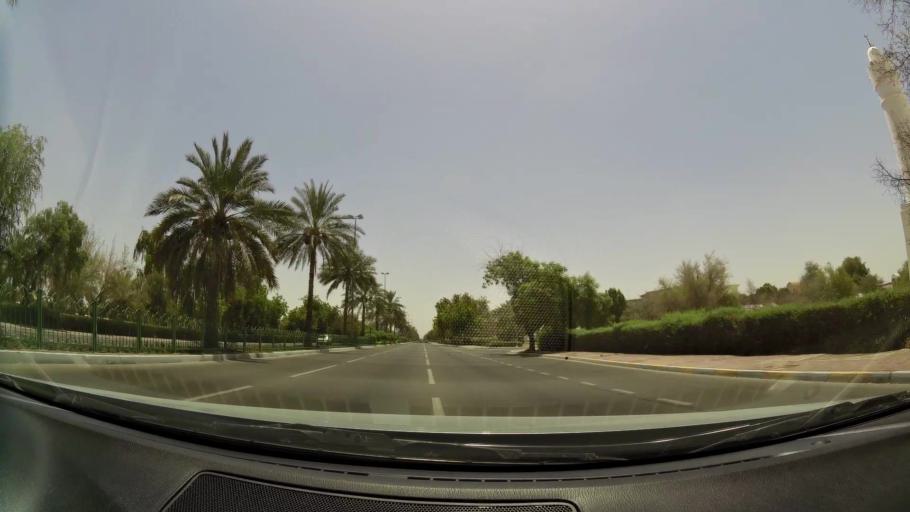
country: OM
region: Al Buraimi
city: Al Buraymi
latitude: 24.2705
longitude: 55.7497
